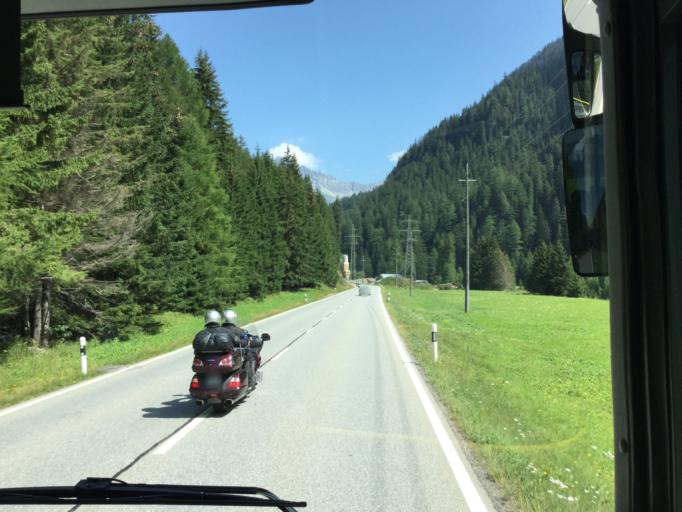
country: CH
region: Grisons
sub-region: Albula District
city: Tiefencastel
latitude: 46.5329
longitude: 9.6228
